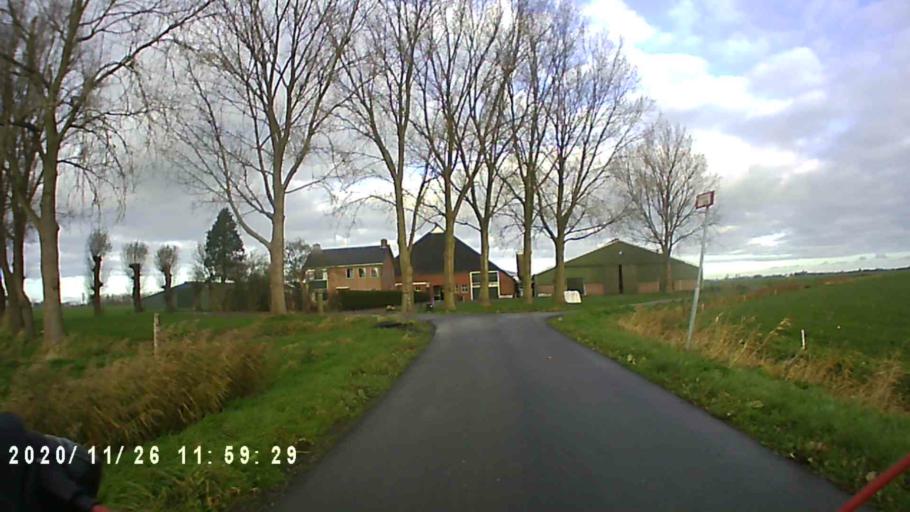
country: NL
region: Groningen
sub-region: Gemeente Bedum
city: Bedum
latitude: 53.3162
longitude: 6.6044
